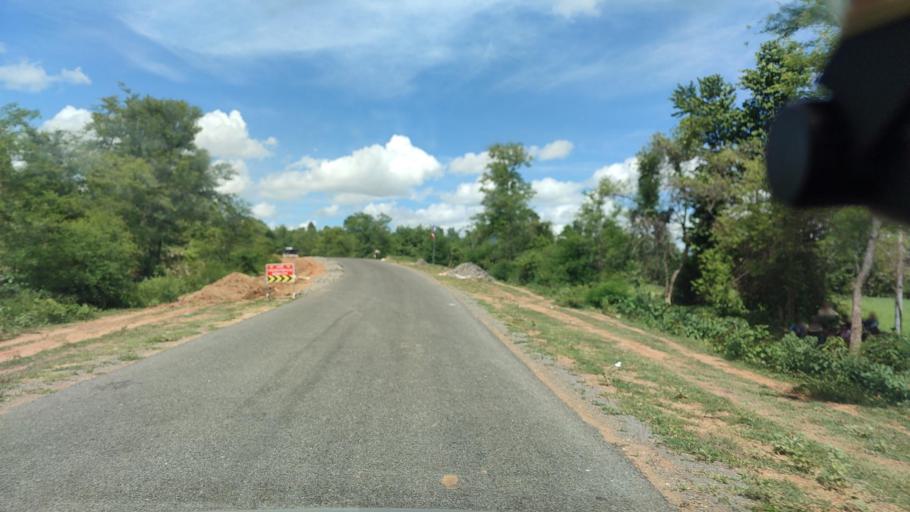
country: MM
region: Magway
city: Magway
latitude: 20.1888
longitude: 95.1939
